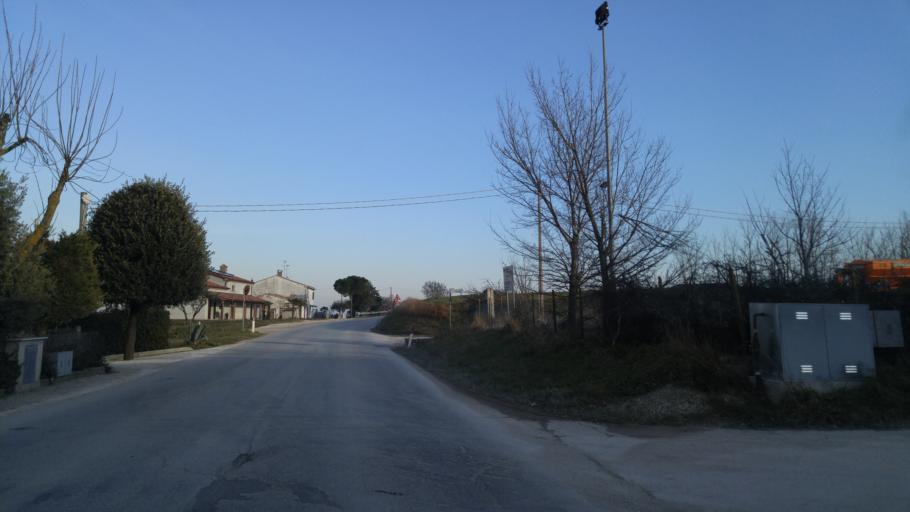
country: IT
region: The Marches
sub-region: Provincia di Pesaro e Urbino
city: San Giorgio di Pesaro
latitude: 43.7283
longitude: 12.9756
